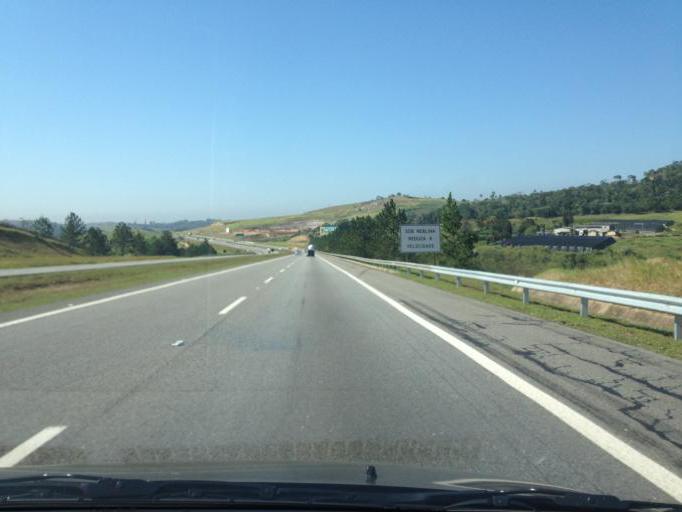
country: BR
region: Sao Paulo
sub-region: Guararema
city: Guararema
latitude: -23.3596
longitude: -46.0849
